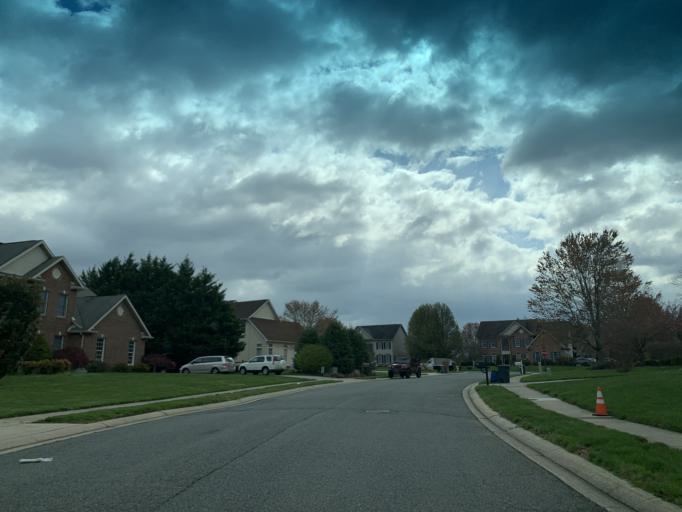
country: US
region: Maryland
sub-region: Harford County
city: South Bel Air
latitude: 39.5567
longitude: -76.3090
